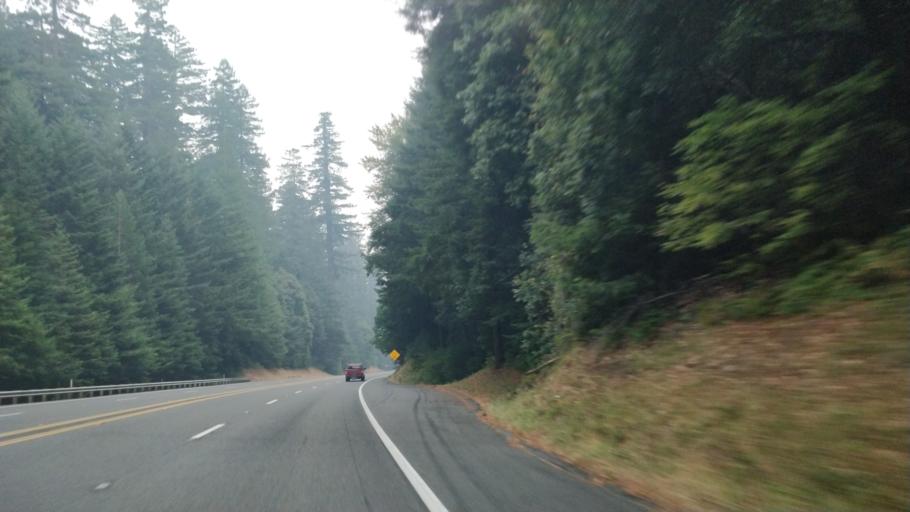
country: US
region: California
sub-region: Humboldt County
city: Rio Dell
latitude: 40.3670
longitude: -123.9234
